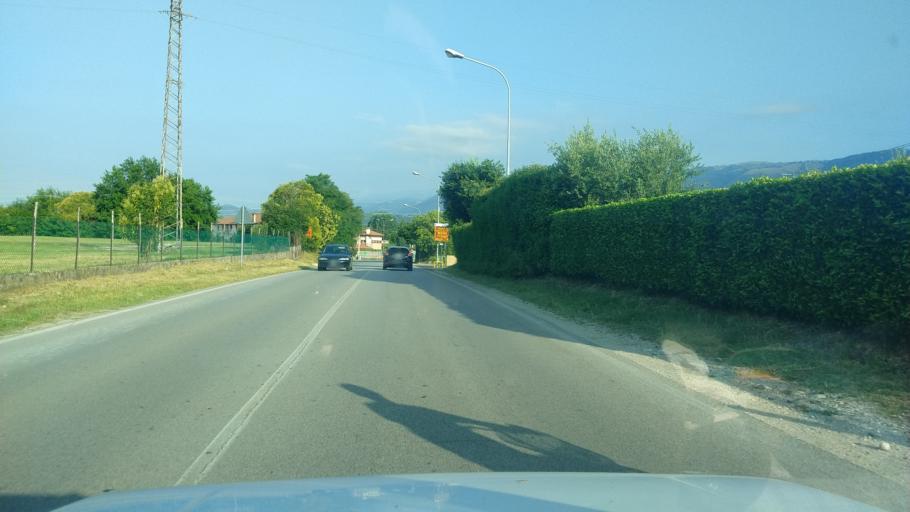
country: IT
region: Veneto
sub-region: Provincia di Vicenza
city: Bassano del Grappa
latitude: 45.7481
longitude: 11.7253
